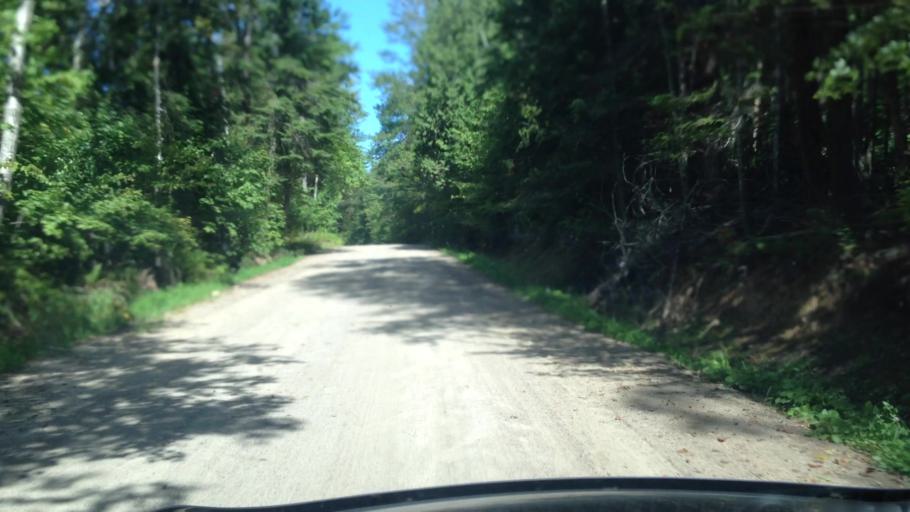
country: CA
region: Quebec
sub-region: Laurentides
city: Brownsburg-Chatham
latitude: 45.9218
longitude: -74.5808
